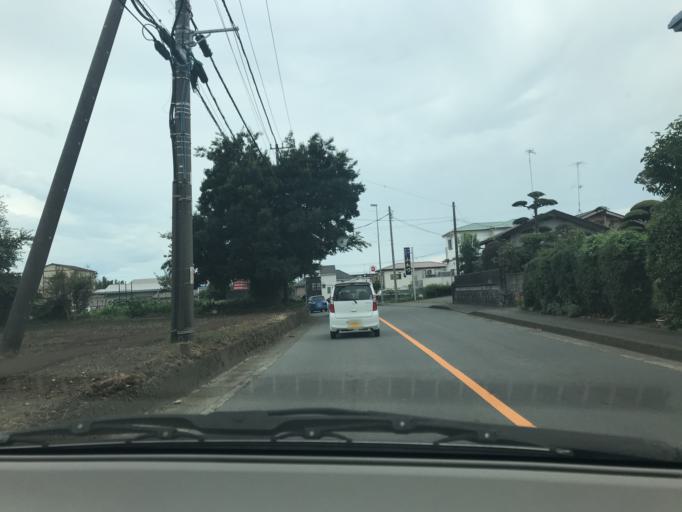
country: JP
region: Kanagawa
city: Fujisawa
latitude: 35.3861
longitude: 139.4393
